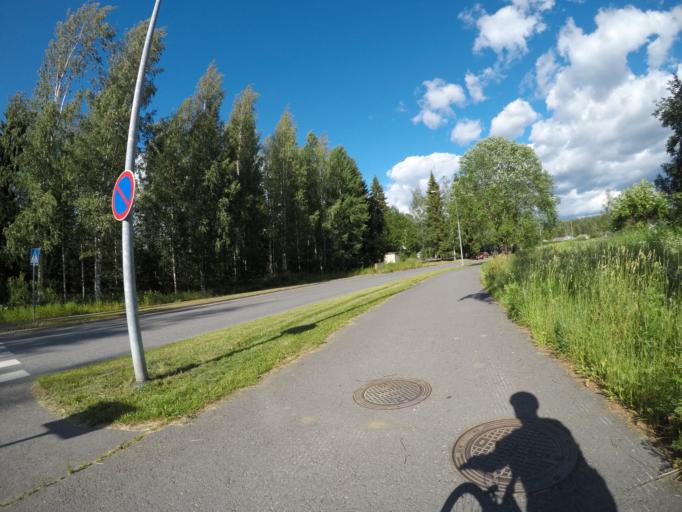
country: FI
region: Haeme
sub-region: Haemeenlinna
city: Haemeenlinna
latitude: 61.0196
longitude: 24.5139
